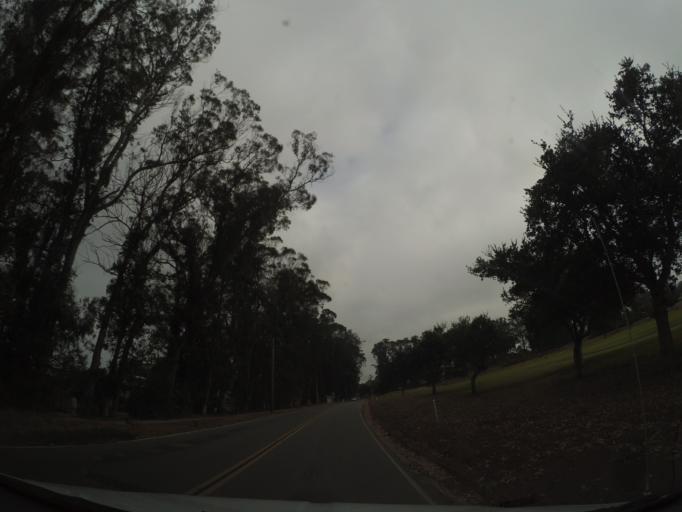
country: US
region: California
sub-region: San Luis Obispo County
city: Morro Bay
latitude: 35.3522
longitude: -120.8436
